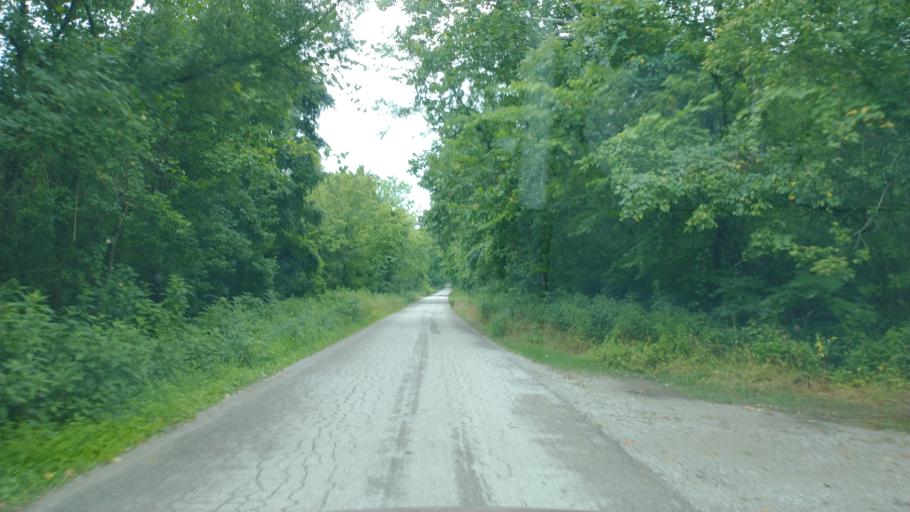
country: US
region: Ohio
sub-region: Meigs County
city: Middleport
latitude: 38.9317
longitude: -82.0705
